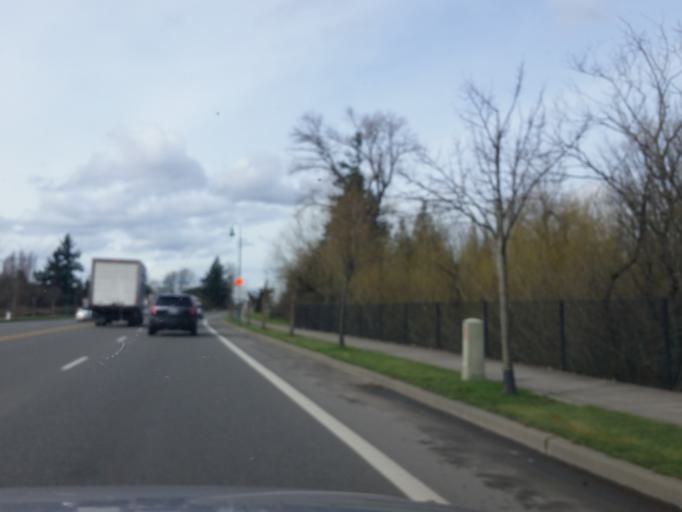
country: US
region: Washington
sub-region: Pierce County
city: Milton
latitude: 47.2214
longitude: -122.3226
